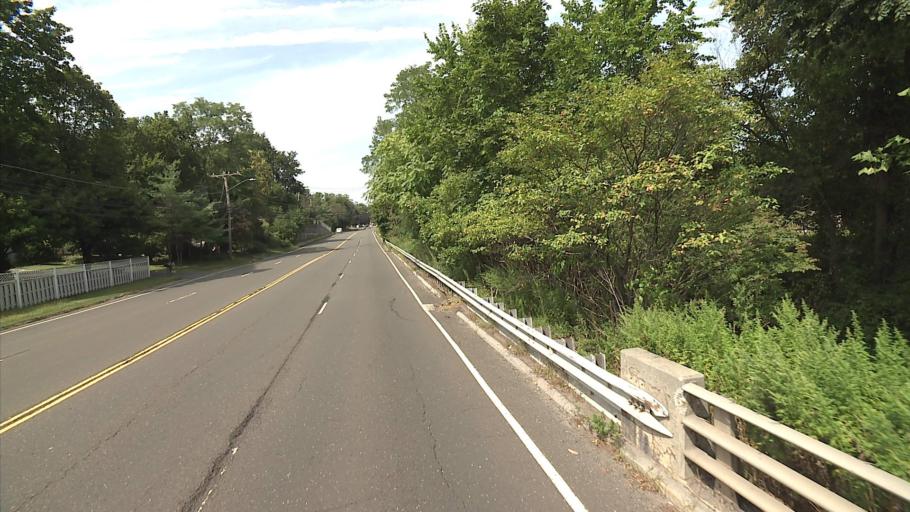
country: US
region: Connecticut
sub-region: Fairfield County
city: Stamford
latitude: 41.0858
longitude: -73.5568
